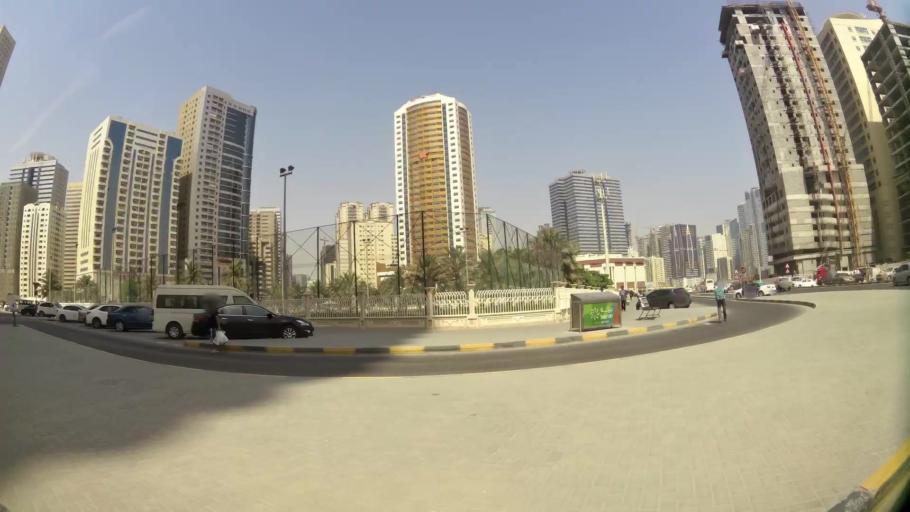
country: AE
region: Ash Shariqah
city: Sharjah
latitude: 25.3030
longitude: 55.3765
